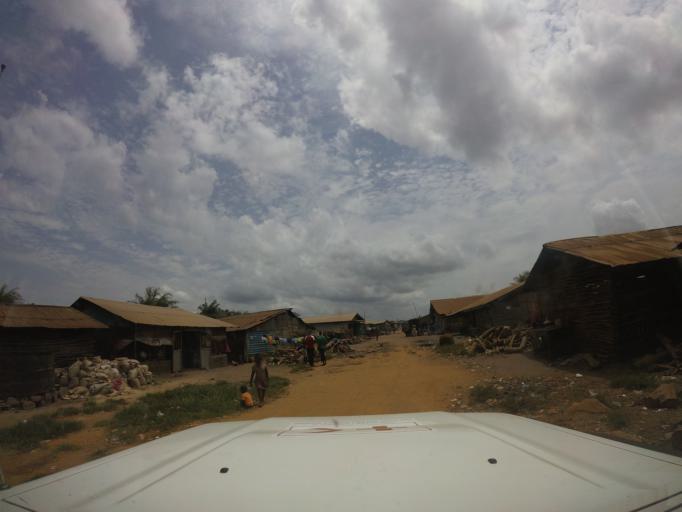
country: LR
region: Grand Cape Mount
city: Robertsport
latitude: 6.7566
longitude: -11.3547
